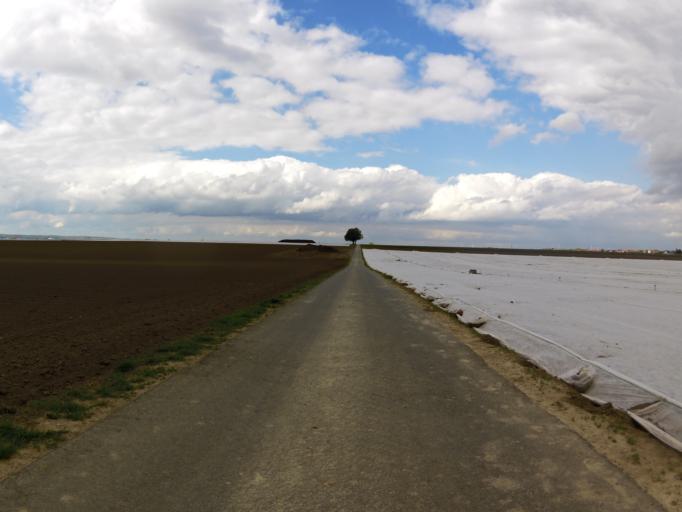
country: DE
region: Bavaria
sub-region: Regierungsbezirk Unterfranken
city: Oberpleichfeld
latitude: 49.8642
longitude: 10.0815
